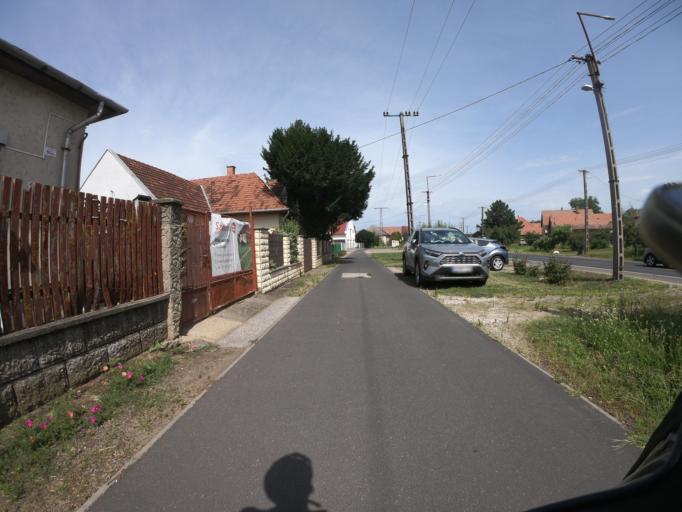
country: HU
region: Jasz-Nagykun-Szolnok
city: Tiszafured
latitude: 47.6130
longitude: 20.7499
